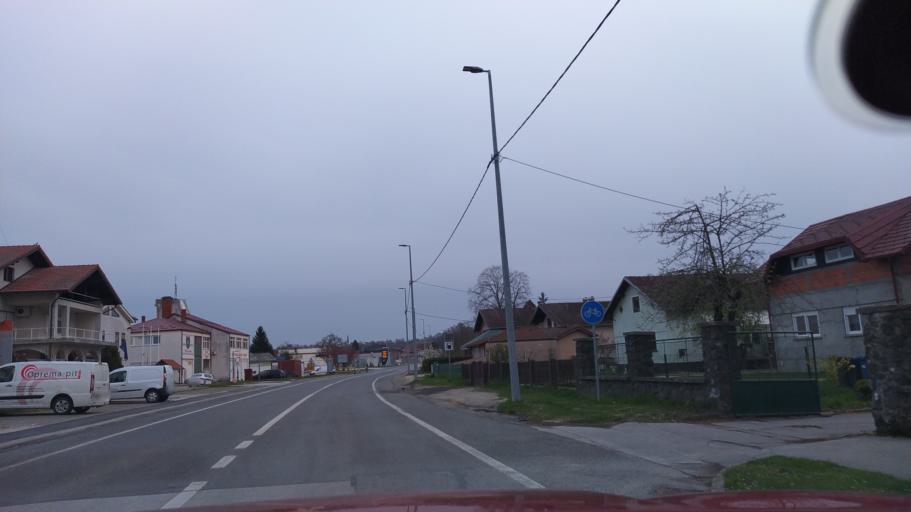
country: HR
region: Varazdinska
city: Ludbreg
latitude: 46.2463
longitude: 16.6217
